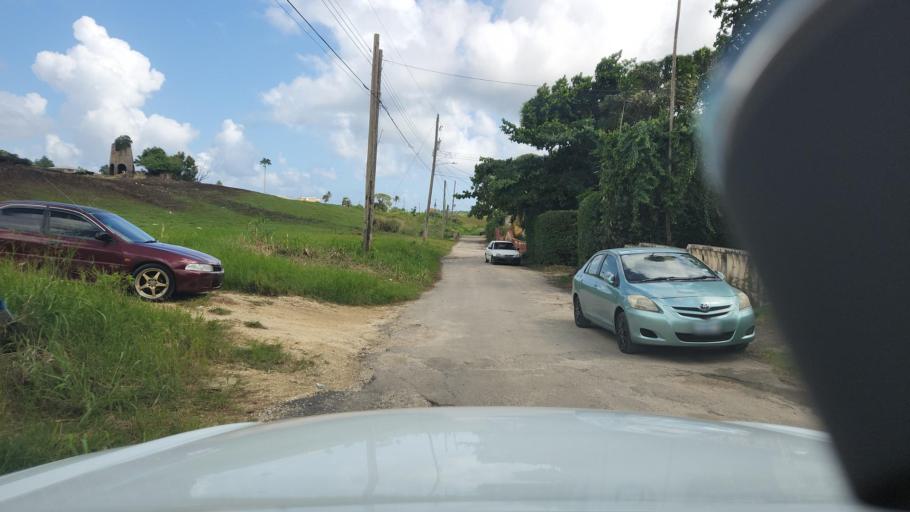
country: BB
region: Saint John
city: Four Cross Roads
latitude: 13.1784
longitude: -59.5061
